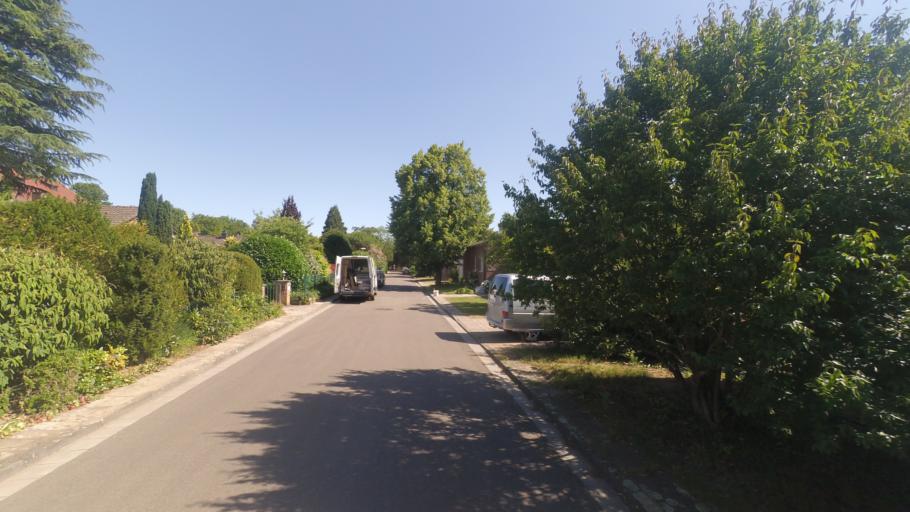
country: DE
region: Rheinland-Pfalz
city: Limburgerhof
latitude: 49.4179
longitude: 8.3945
